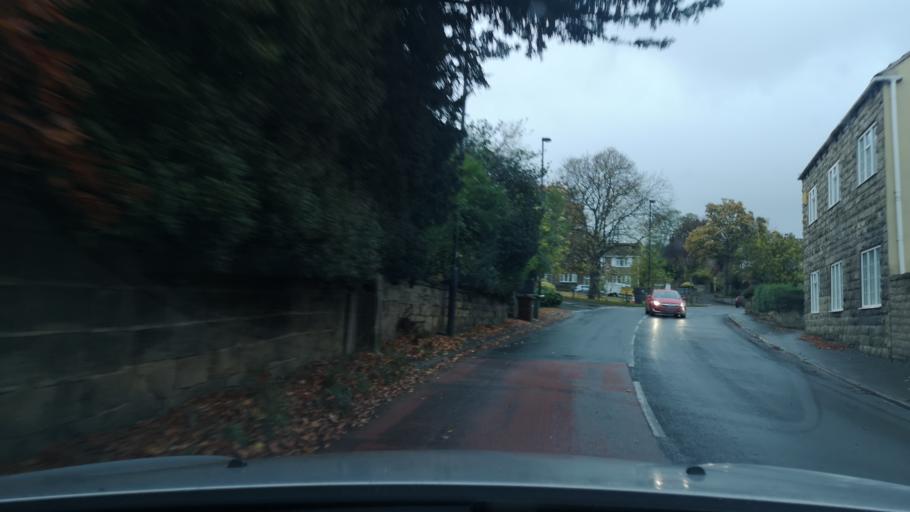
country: GB
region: England
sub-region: City and Borough of Wakefield
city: Low Ackworth
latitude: 53.6559
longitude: -1.3352
